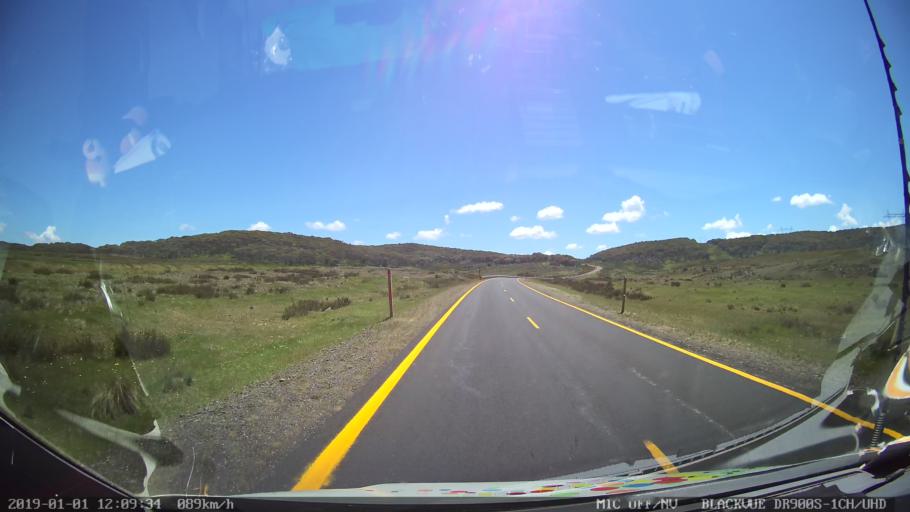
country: AU
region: New South Wales
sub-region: Tumut Shire
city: Tumut
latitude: -35.8054
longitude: 148.4960
